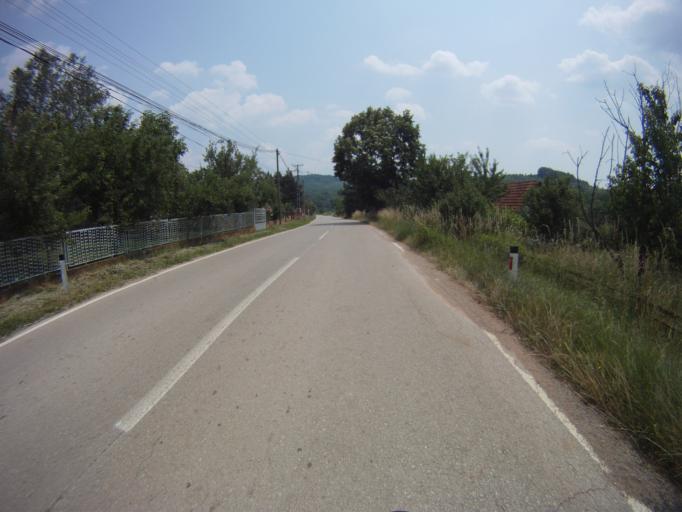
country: RS
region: Central Serbia
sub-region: Nisavski Okrug
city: Gadzin Han
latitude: 43.2066
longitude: 21.9891
